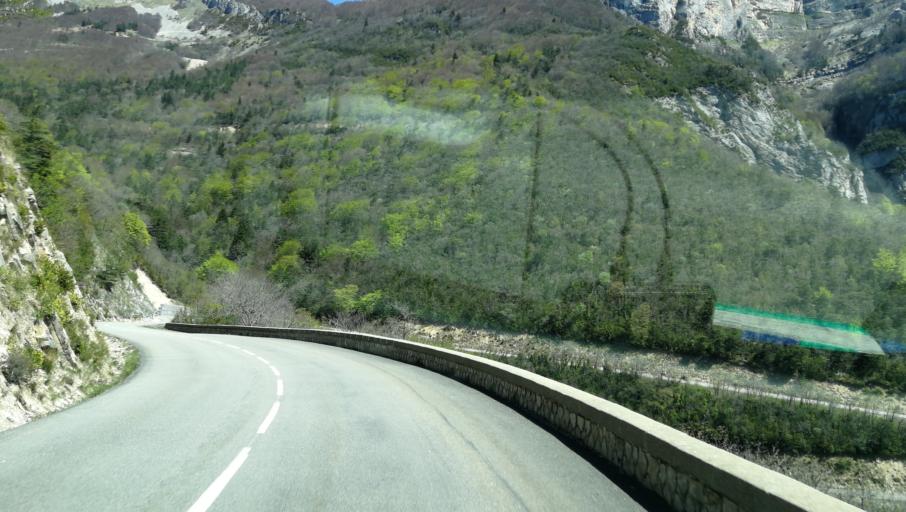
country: FR
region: Rhone-Alpes
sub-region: Departement de la Drome
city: Die
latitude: 44.8258
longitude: 5.3943
